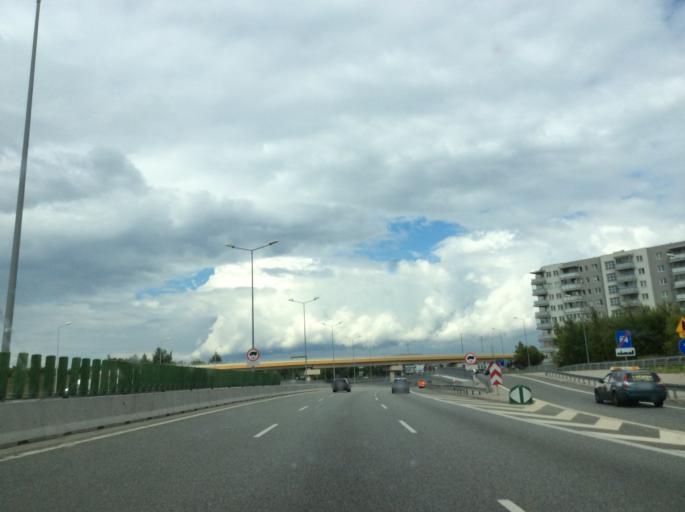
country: PL
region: Masovian Voivodeship
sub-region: Warszawa
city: Bemowo
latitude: 52.2423
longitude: 20.8919
